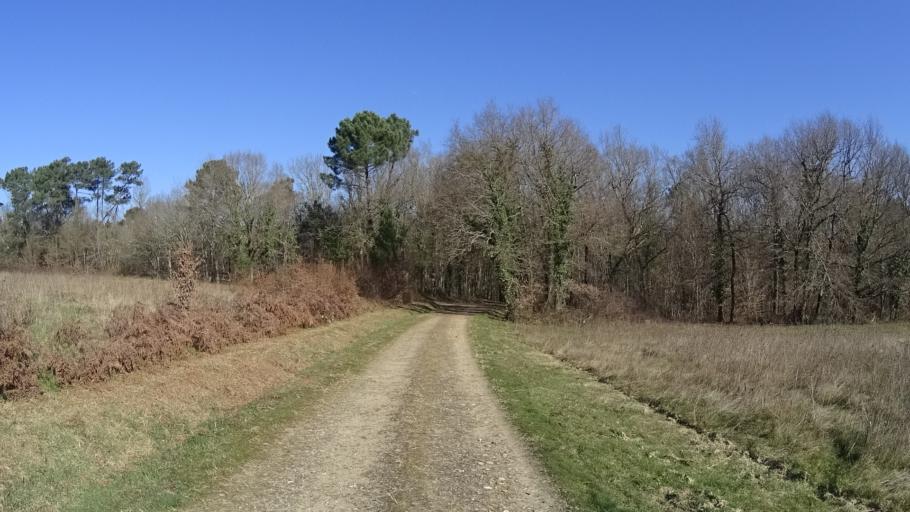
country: FR
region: Aquitaine
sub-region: Departement de la Dordogne
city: Saint-Medard-de-Mussidan
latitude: 45.0462
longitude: 0.2549
